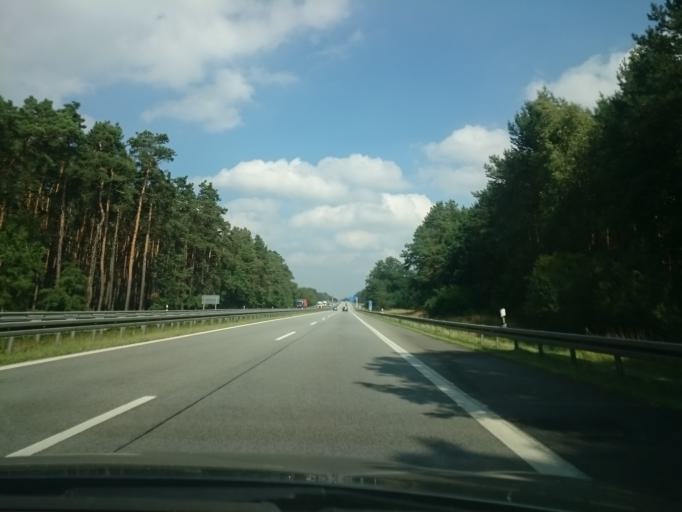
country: DE
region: Brandenburg
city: Althuttendorf
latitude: 52.9334
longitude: 13.7877
